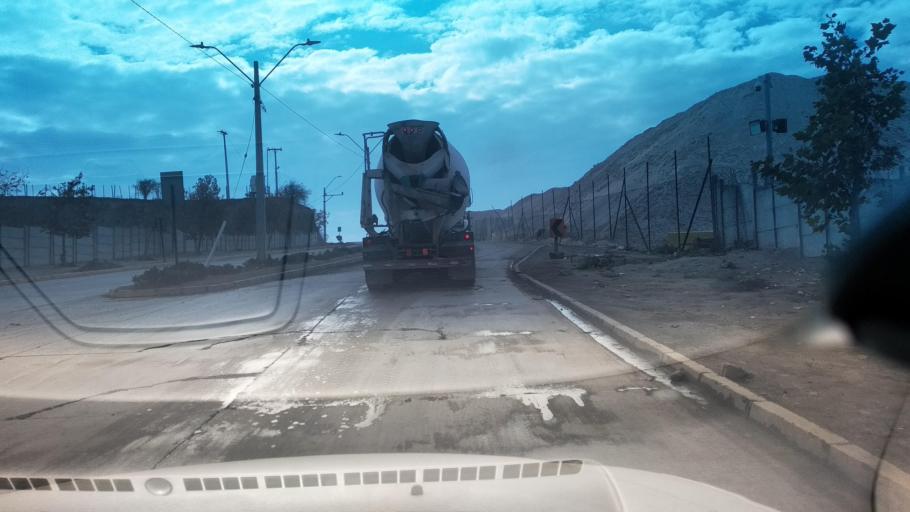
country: CL
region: Santiago Metropolitan
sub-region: Provincia de Santiago
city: Lo Prado
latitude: -33.4539
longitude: -70.7982
